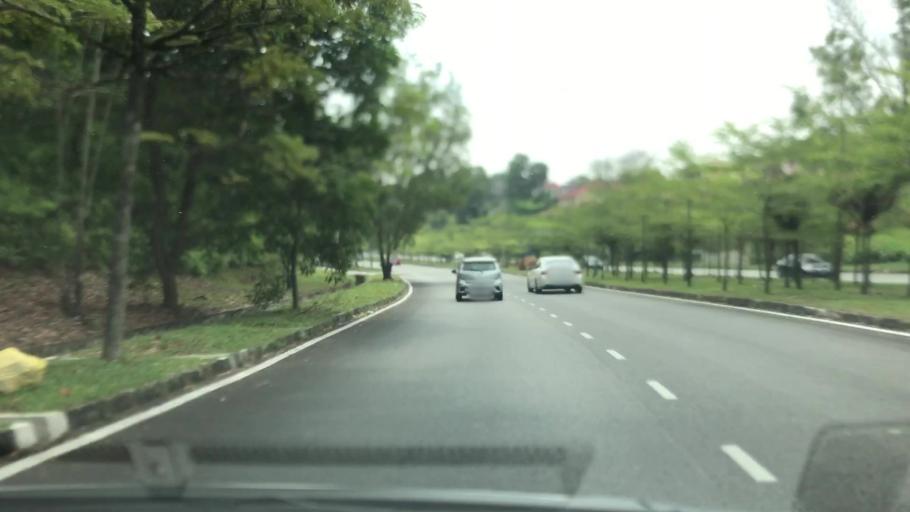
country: MY
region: Putrajaya
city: Putrajaya
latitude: 3.0054
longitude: 101.6684
